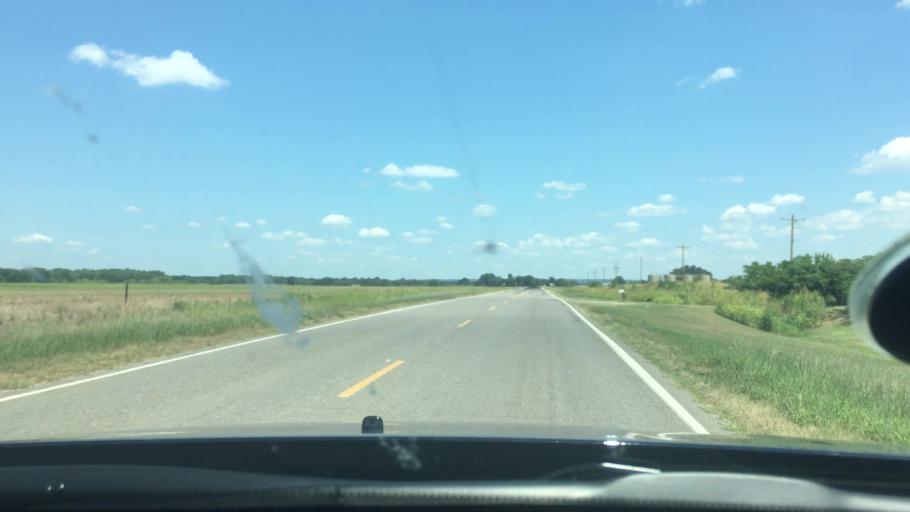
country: US
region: Oklahoma
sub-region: Carter County
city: Dickson
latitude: 34.2189
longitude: -96.9771
